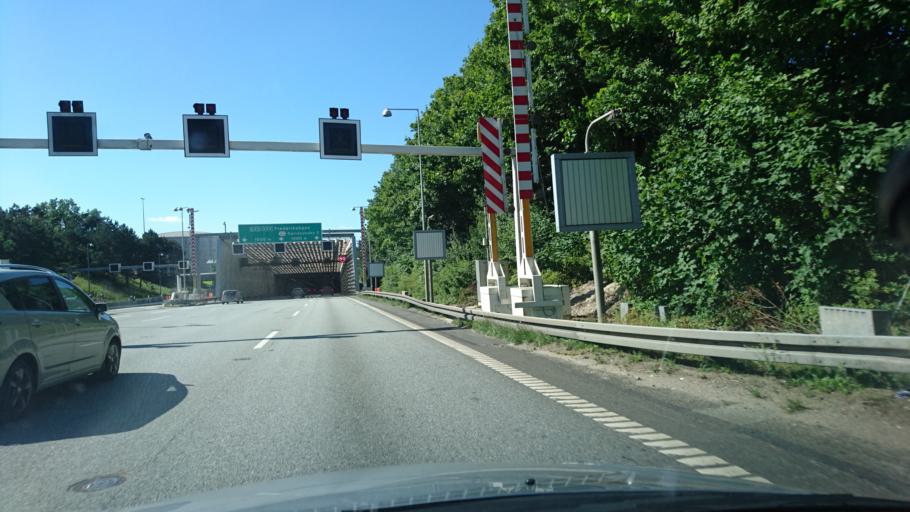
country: DK
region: North Denmark
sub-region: Alborg Kommune
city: Aalborg
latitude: 57.0528
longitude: 9.9660
